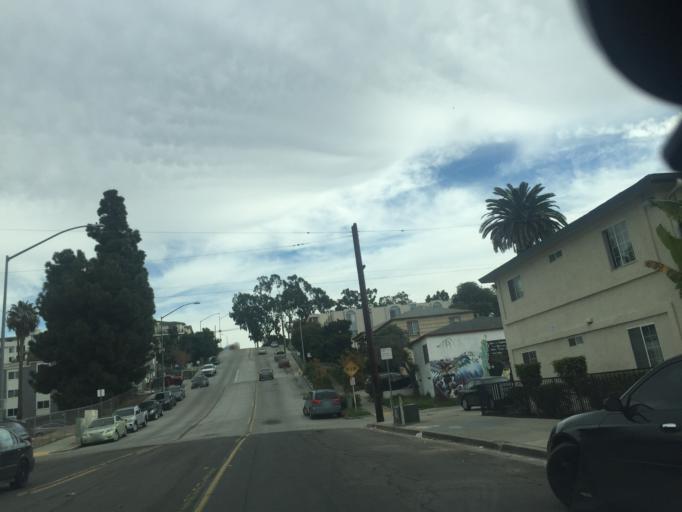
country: US
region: California
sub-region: San Diego County
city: Lemon Grove
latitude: 32.7530
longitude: -117.0857
